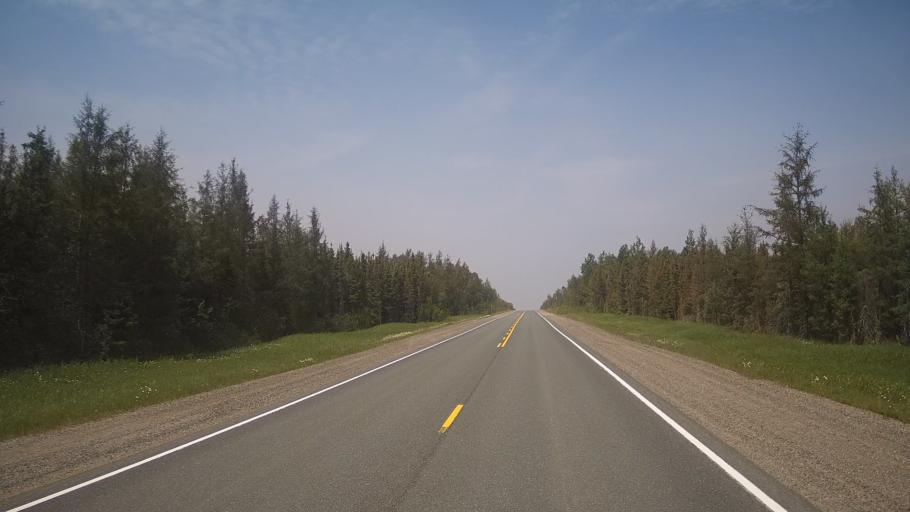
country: CA
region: Ontario
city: Timmins
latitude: 48.7713
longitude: -81.3629
